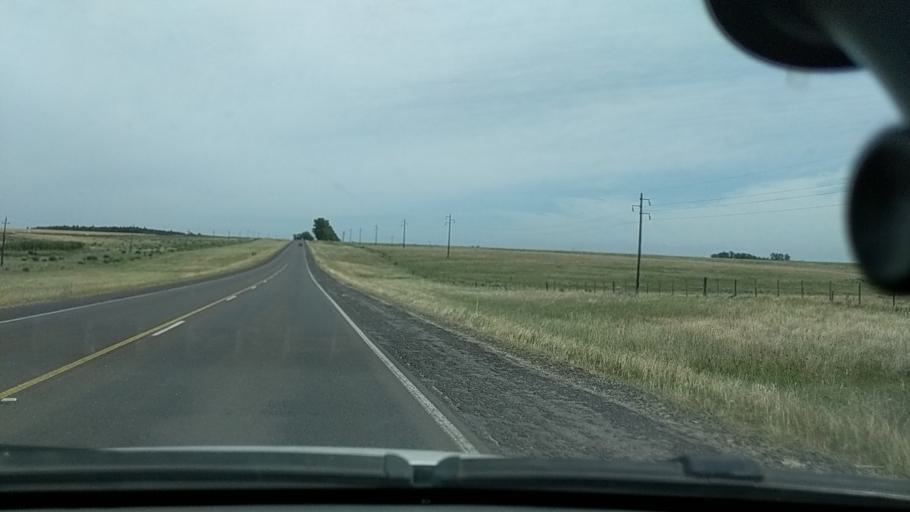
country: UY
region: Durazno
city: Durazno
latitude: -33.4818
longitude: -56.4432
